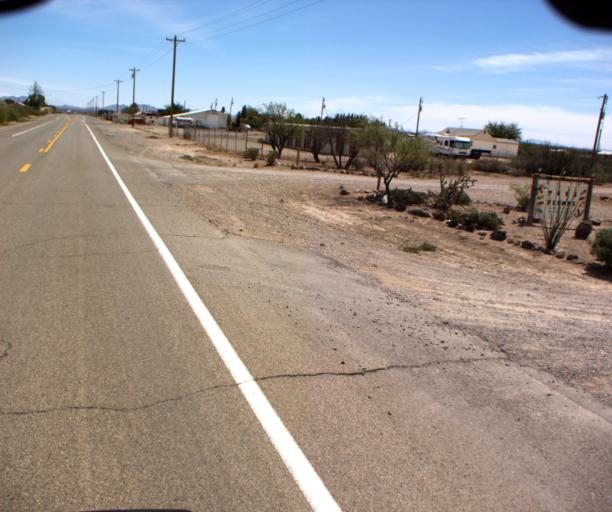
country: US
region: New Mexico
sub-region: Hidalgo County
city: Lordsburg
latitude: 32.2678
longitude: -109.2325
